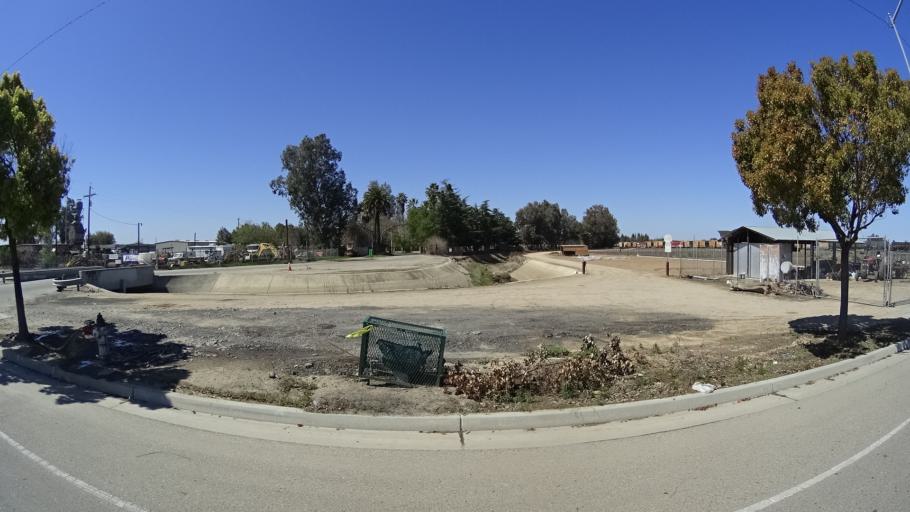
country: US
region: California
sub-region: Fresno County
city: West Park
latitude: 36.7449
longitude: -119.8445
